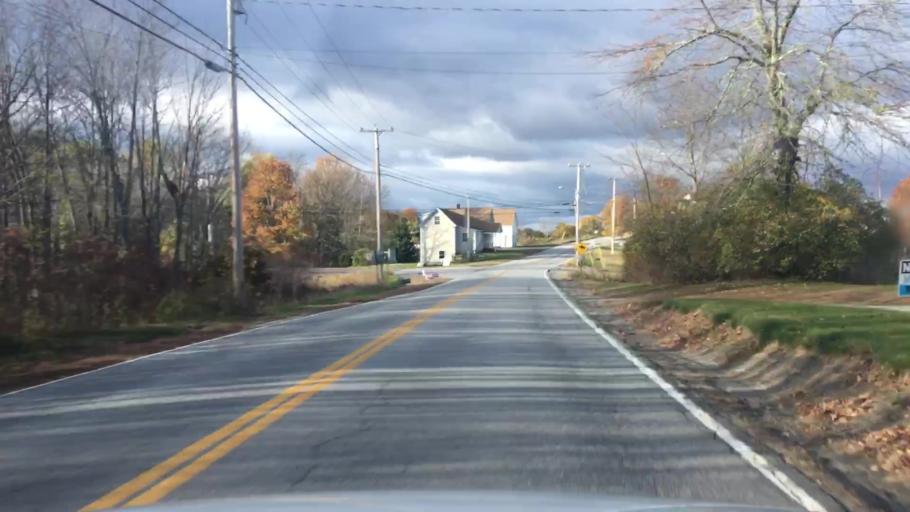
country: US
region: Maine
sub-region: Androscoggin County
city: Leeds
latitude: 44.3027
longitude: -70.1188
